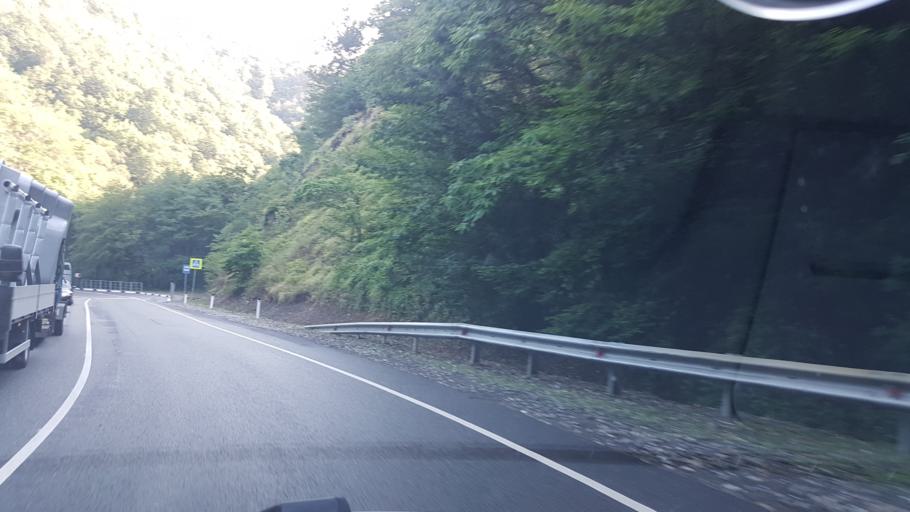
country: RU
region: Krasnodarskiy
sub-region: Sochi City
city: Lazarevskoye
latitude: 43.8379
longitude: 39.4219
